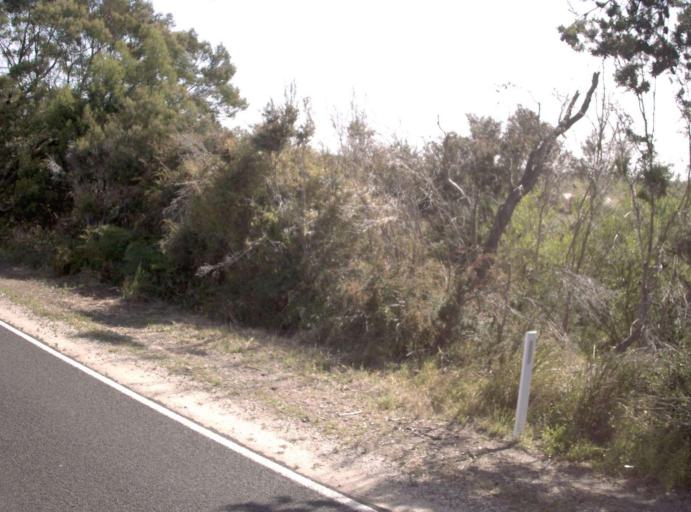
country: AU
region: Victoria
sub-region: Wellington
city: Sale
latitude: -38.3527
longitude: 147.1713
